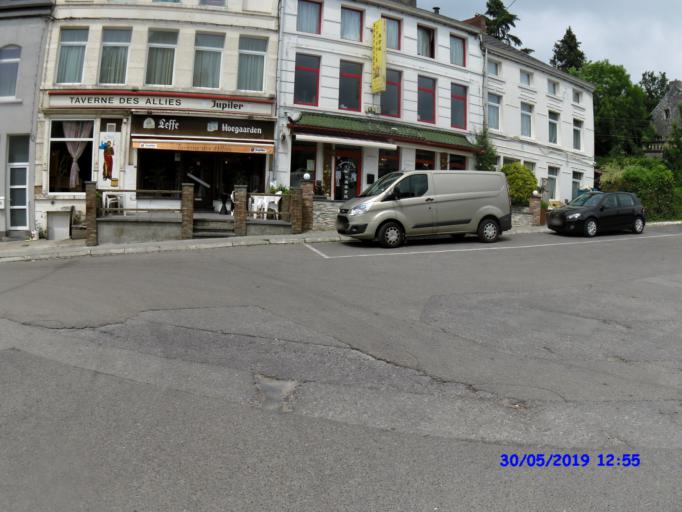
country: BE
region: Wallonia
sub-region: Province du Hainaut
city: Thuin
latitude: 50.3422
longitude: 4.2874
